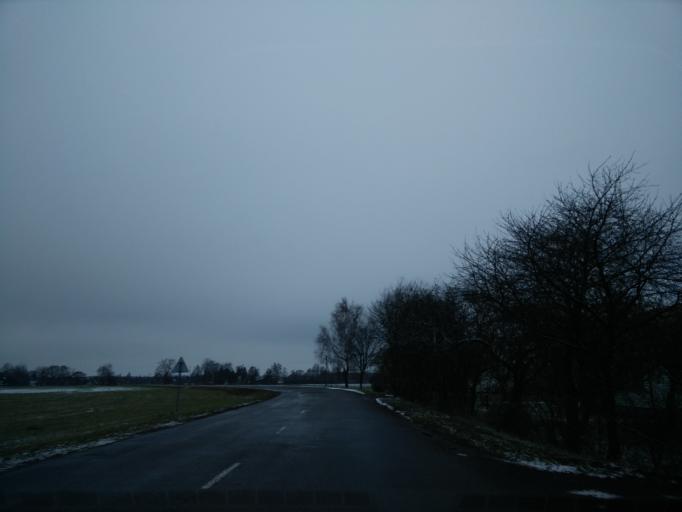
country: LT
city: Ariogala
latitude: 55.3839
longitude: 23.3476
